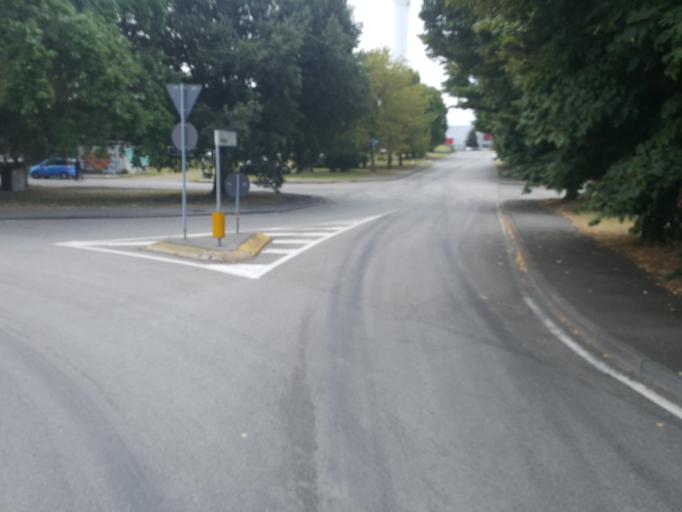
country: IT
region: Lombardy
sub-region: Provincia di Monza e Brianza
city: Cavenago di Brianza
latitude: 45.5804
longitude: 9.4014
